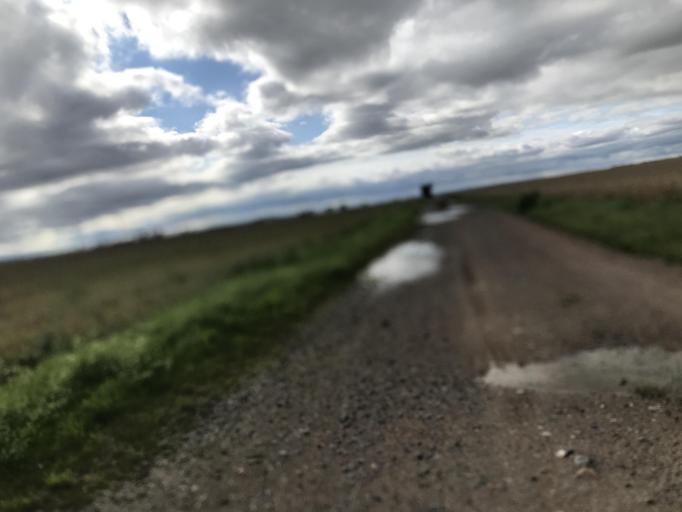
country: DE
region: Saxony-Anhalt
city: Ditfurt
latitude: 51.8097
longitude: 11.2394
